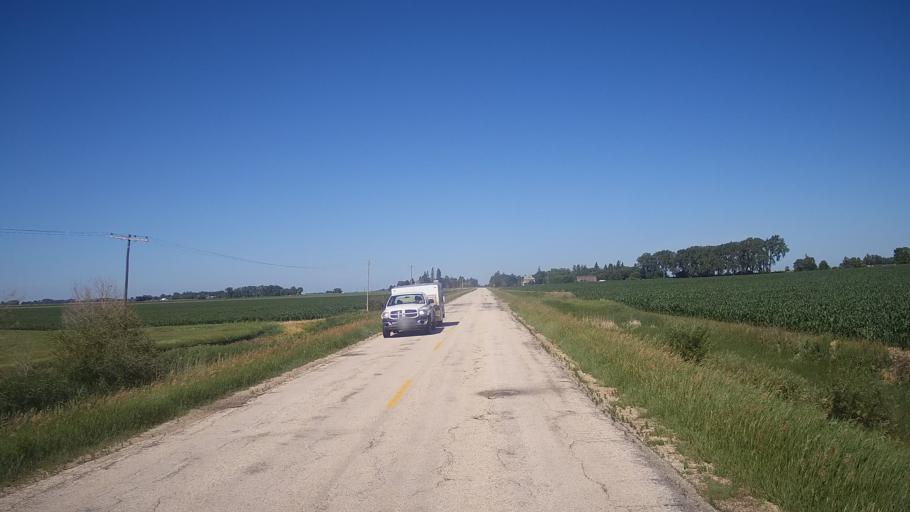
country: CA
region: Manitoba
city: Portage la Prairie
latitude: 50.0437
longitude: -98.0463
